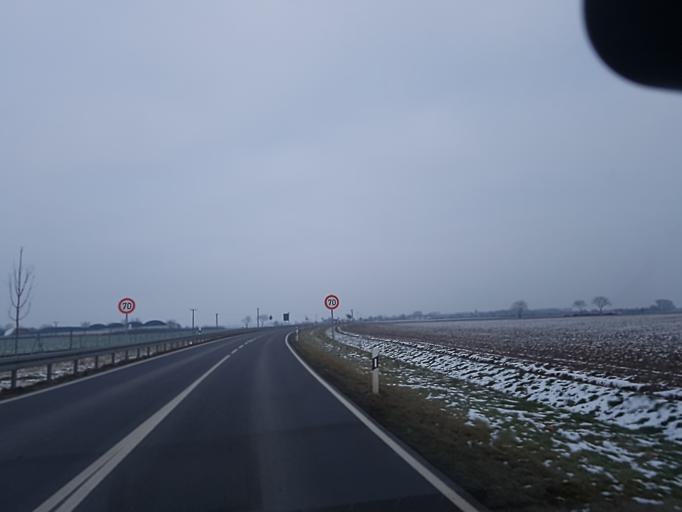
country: DE
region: Saxony
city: Naundorf
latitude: 51.2487
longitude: 13.0889
